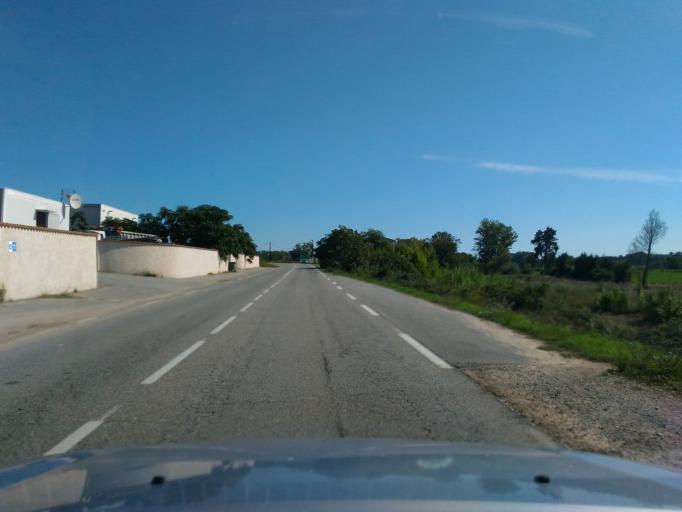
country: FR
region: Corsica
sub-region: Departement de la Haute-Corse
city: Aleria
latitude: 42.1131
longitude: 9.5064
